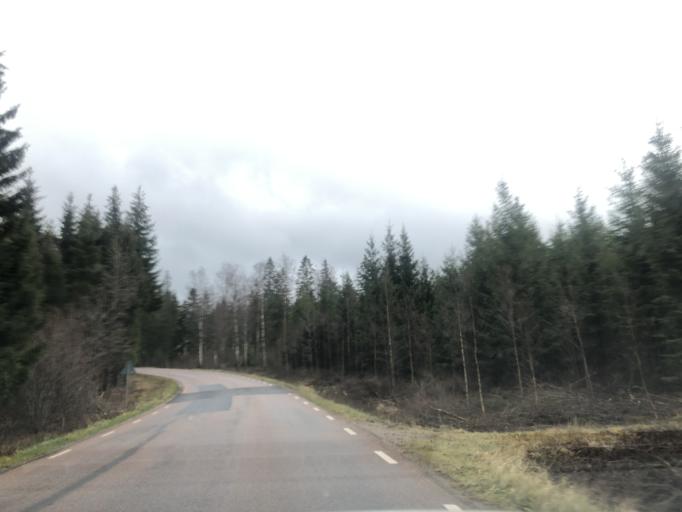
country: SE
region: Vaestra Goetaland
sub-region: Ulricehamns Kommun
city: Ulricehamn
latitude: 57.8319
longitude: 13.4840
